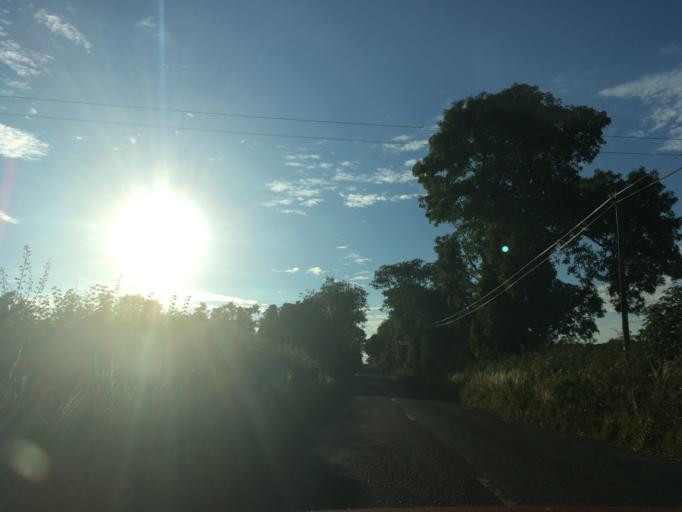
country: IE
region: Munster
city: Cashel
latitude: 52.4459
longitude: -7.8969
